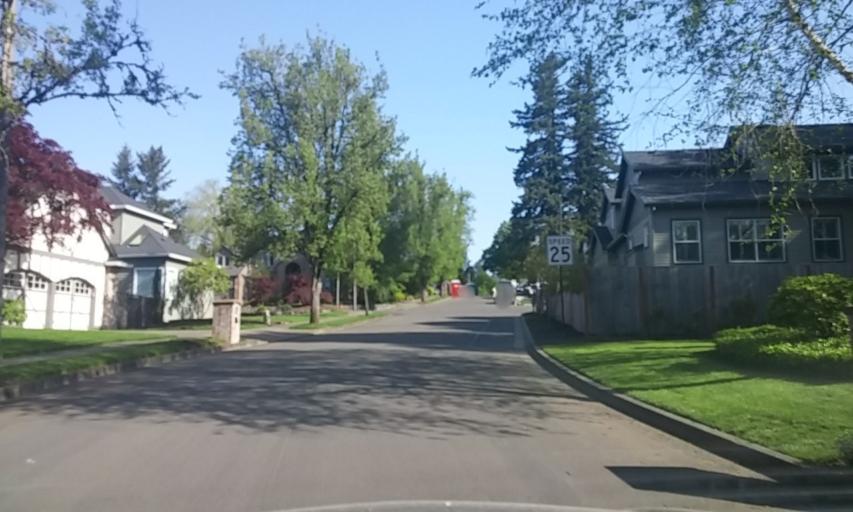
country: US
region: Oregon
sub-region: Washington County
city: Durham
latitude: 45.4266
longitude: -122.7359
